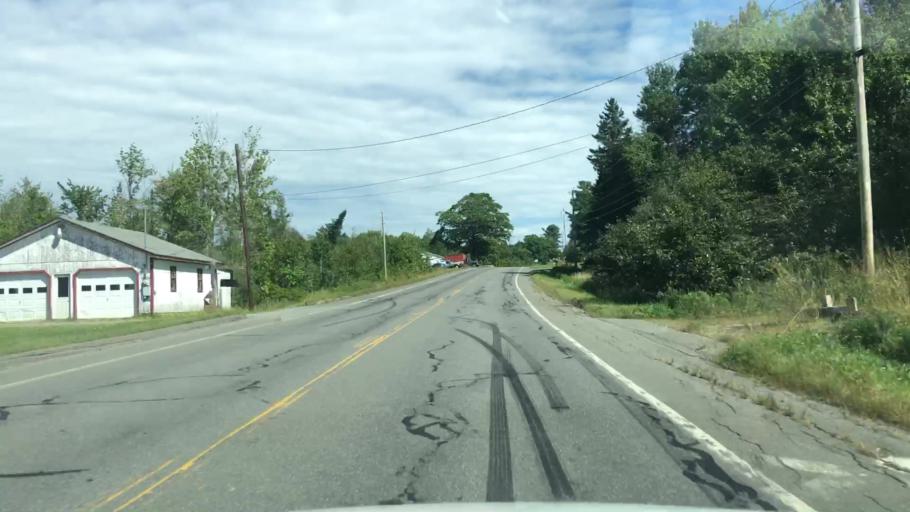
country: US
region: Maine
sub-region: Penobscot County
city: Garland
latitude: 45.0812
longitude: -69.2294
